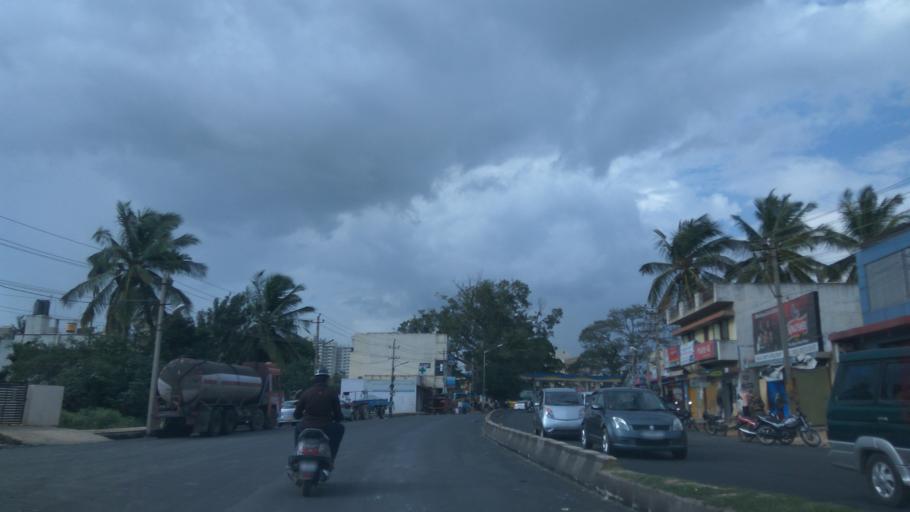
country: IN
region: Karnataka
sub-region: Bangalore Urban
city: Yelahanka
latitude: 13.0549
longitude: 77.6320
